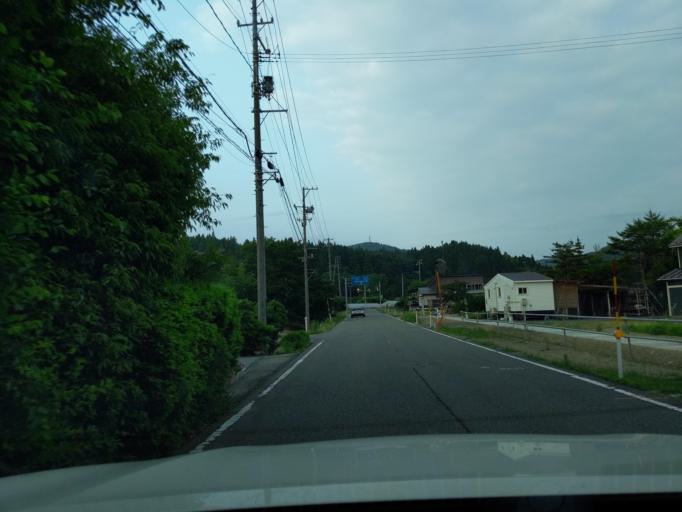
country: JP
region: Niigata
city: Kashiwazaki
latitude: 37.4473
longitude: 138.6638
